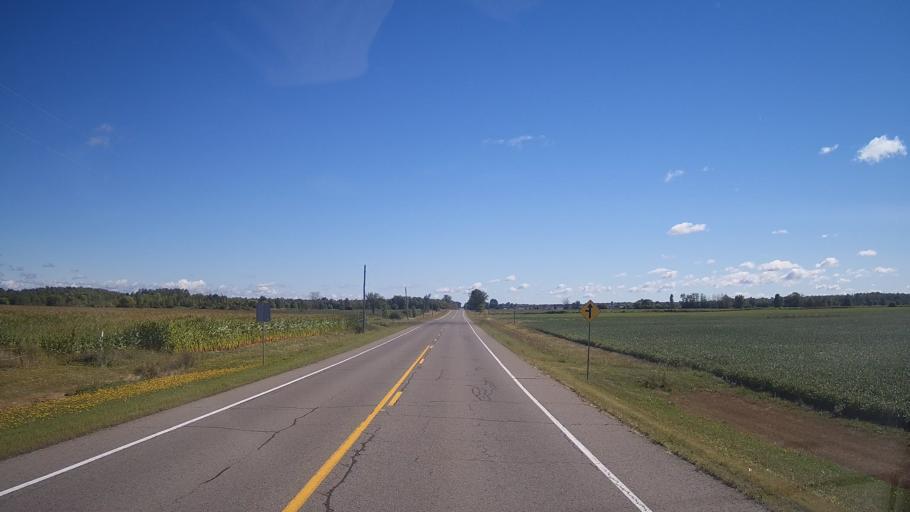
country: CA
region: Ontario
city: Prescott
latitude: 44.9264
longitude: -75.3410
